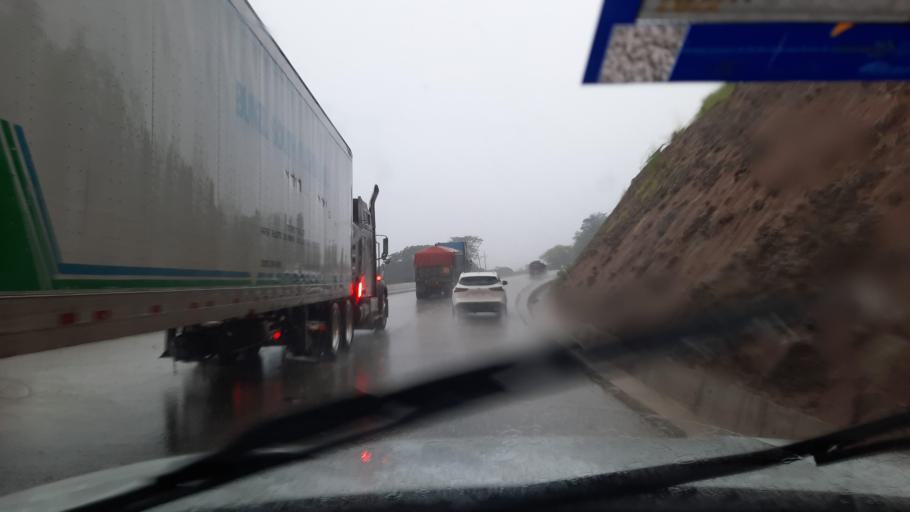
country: CR
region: Guanacaste
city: Juntas
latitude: 10.3251
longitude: -85.0503
